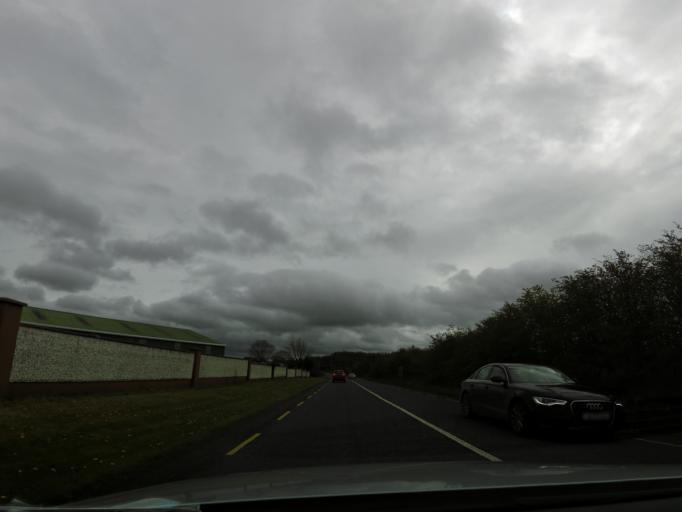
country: IE
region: Leinster
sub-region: Kilkenny
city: Ballyragget
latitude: 52.7283
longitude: -7.3782
